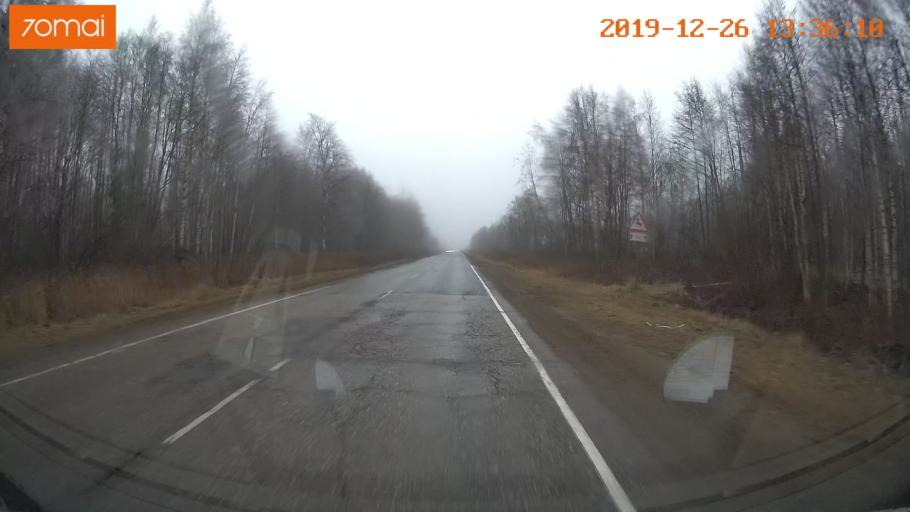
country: RU
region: Vologda
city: Sheksna
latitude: 58.7855
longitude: 38.3511
